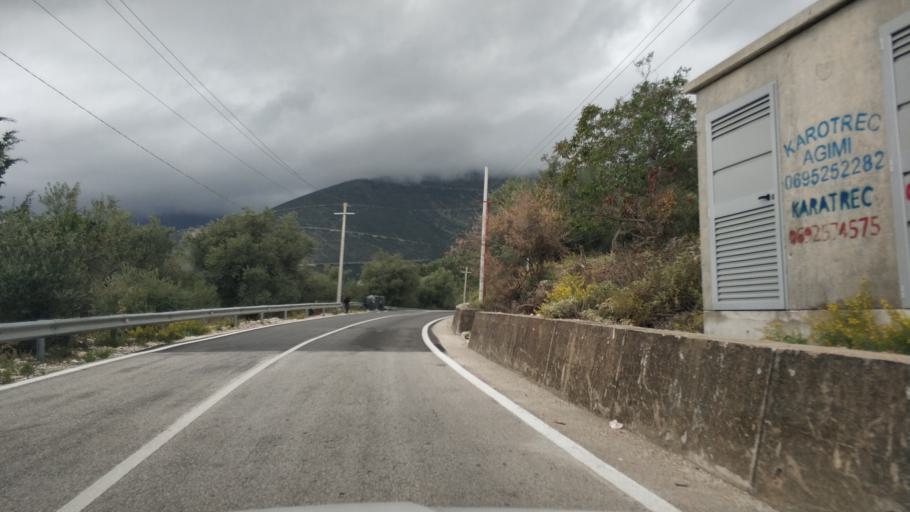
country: AL
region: Vlore
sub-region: Rrethi i Vlores
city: Vranisht
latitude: 40.1654
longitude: 19.6202
